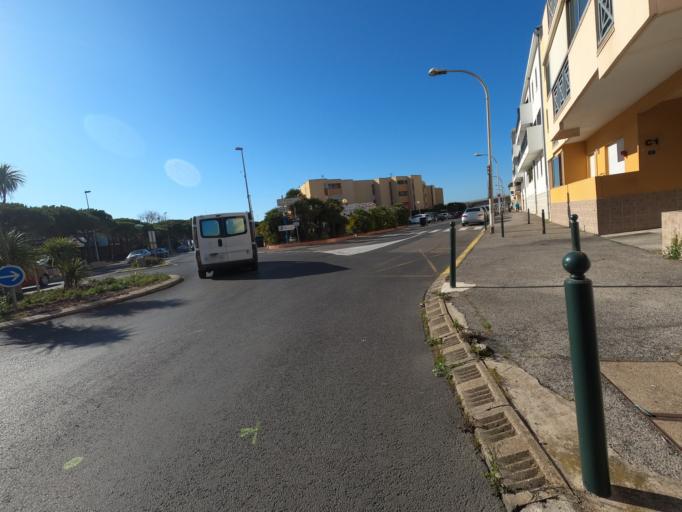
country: FR
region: Languedoc-Roussillon
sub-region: Departement de l'Herault
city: Palavas-les-Flots
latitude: 43.5293
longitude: 3.9253
